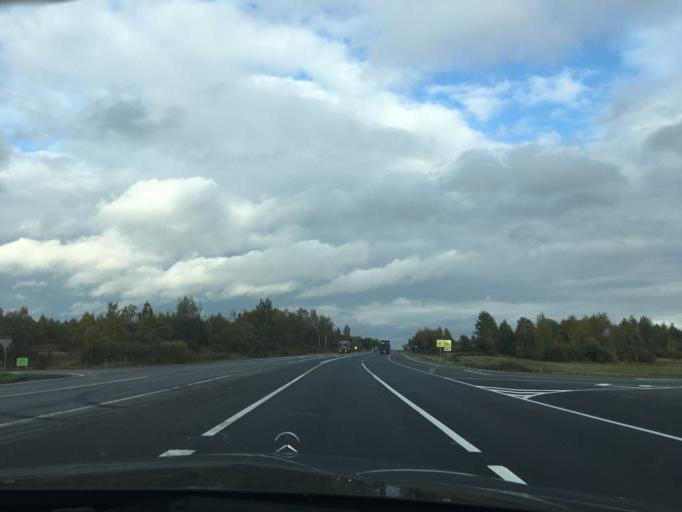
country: BY
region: Vitebsk
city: Dubrowna
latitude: 54.6729
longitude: 30.7212
